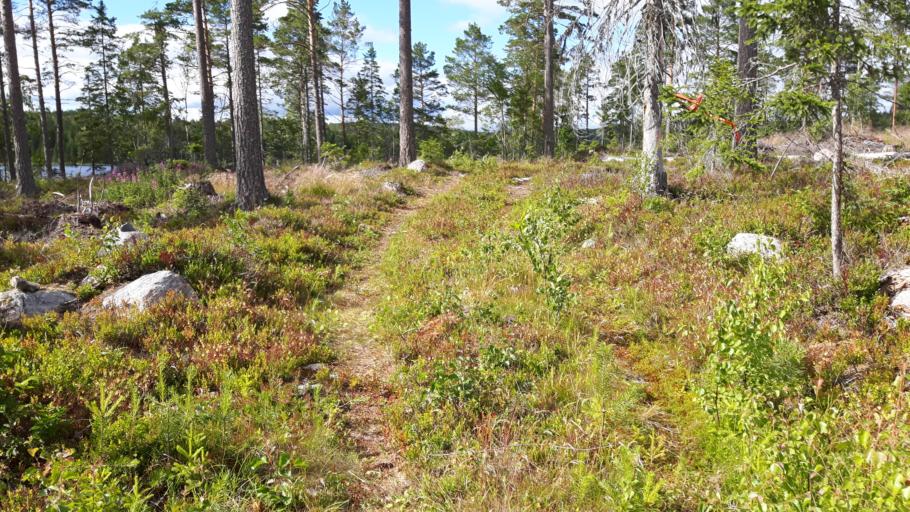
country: SE
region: Vaesternorrland
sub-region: Haernoesands Kommun
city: Haernoesand
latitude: 62.6827
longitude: 18.0462
